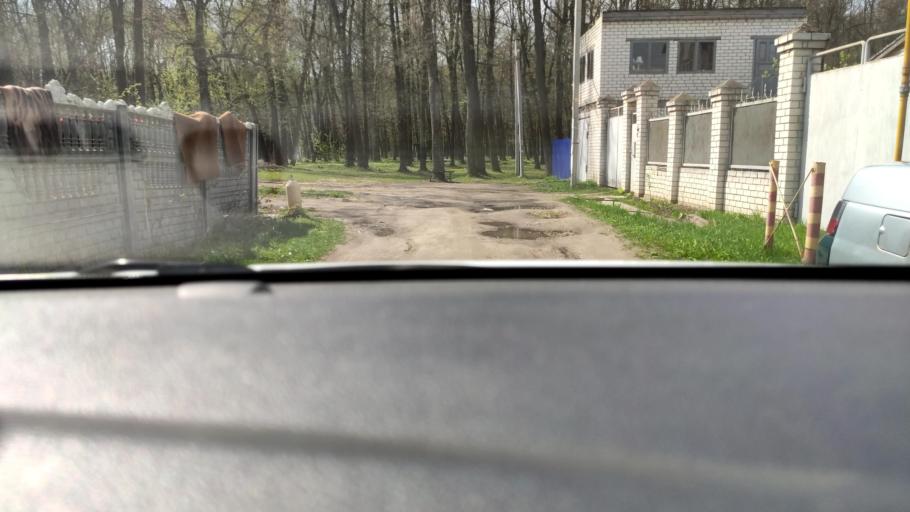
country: RU
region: Tatarstan
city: Osinovo
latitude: 55.8483
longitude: 48.8842
